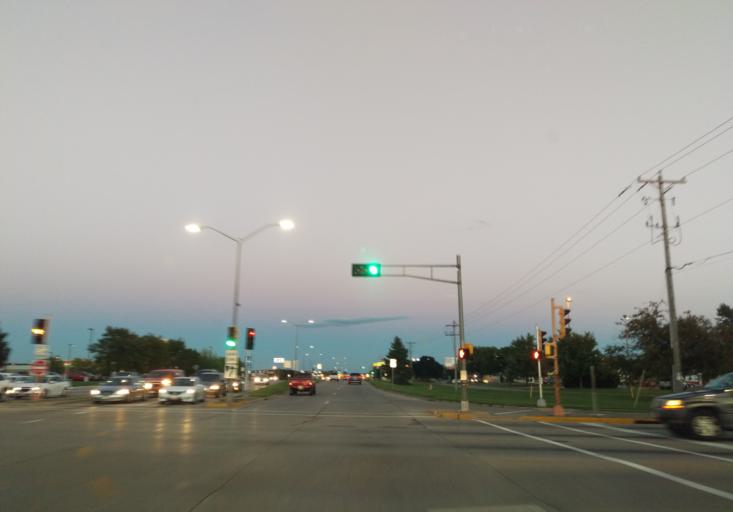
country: US
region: Wisconsin
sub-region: Rock County
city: Janesville
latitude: 42.7201
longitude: -88.9968
